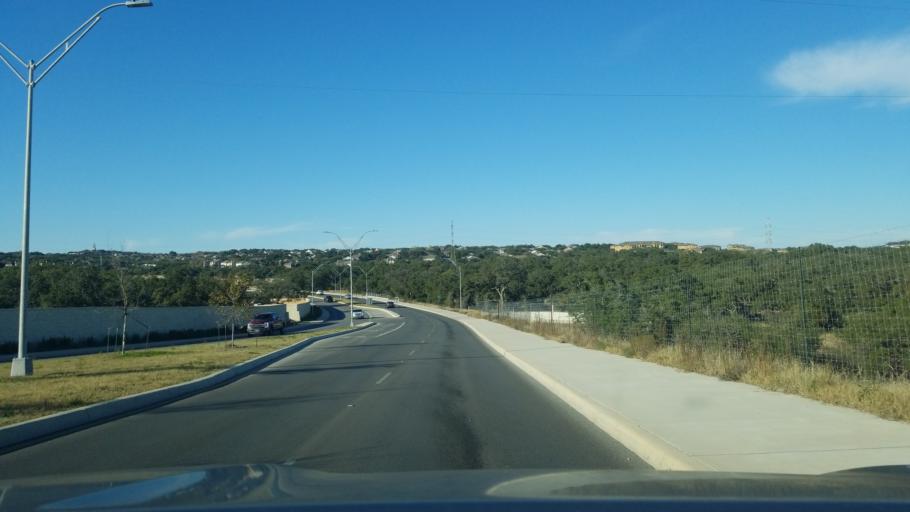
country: US
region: Texas
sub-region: Bexar County
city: Hollywood Park
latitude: 29.6258
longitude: -98.4768
